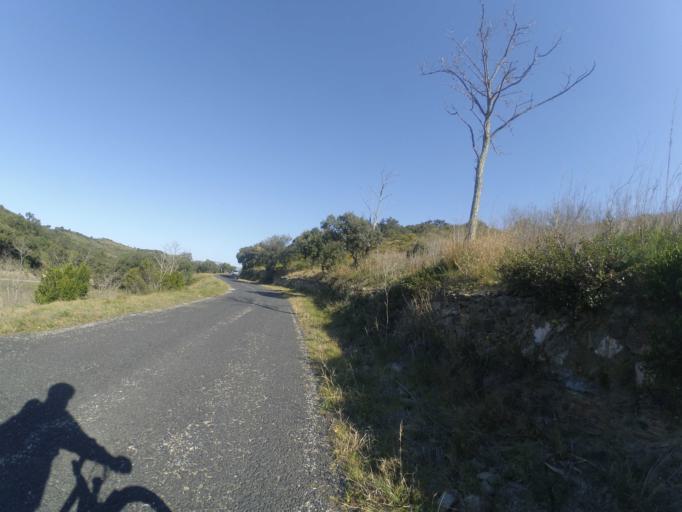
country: FR
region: Languedoc-Roussillon
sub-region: Departement des Pyrenees-Orientales
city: Corneilla-la-Riviere
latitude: 42.7416
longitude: 2.7288
